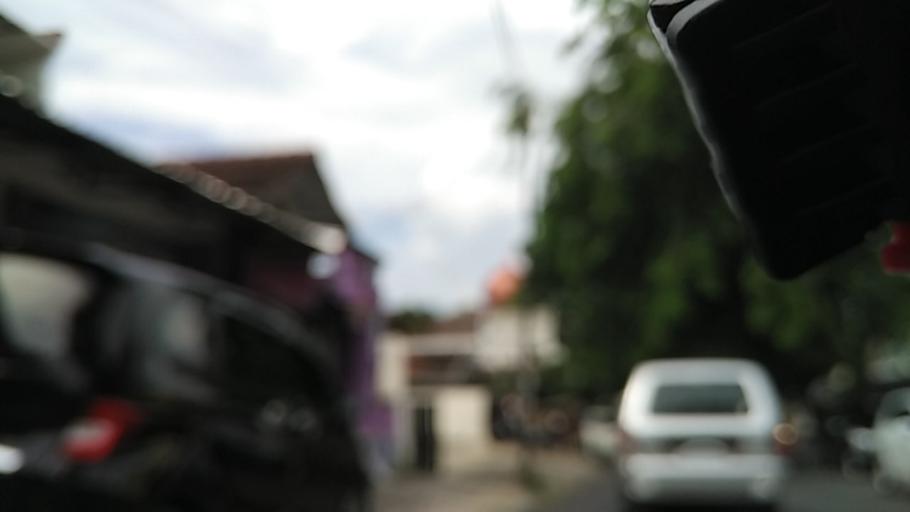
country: ID
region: Central Java
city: Semarang
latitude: -7.0080
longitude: 110.4268
